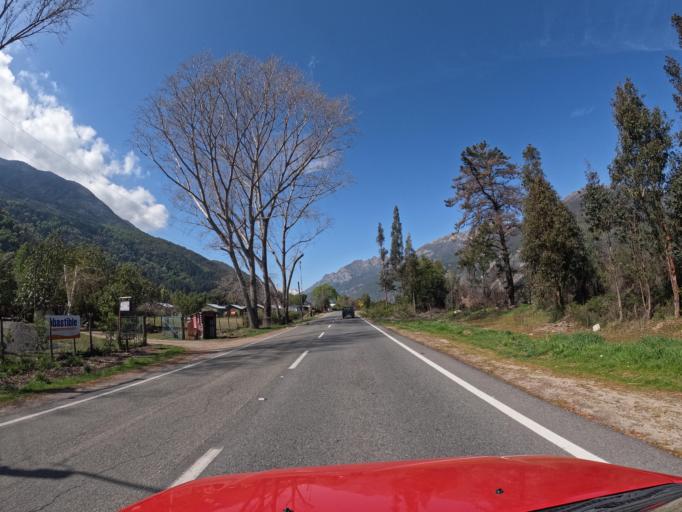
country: CL
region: Maule
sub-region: Provincia de Linares
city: Colbun
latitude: -35.7208
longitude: -71.1791
